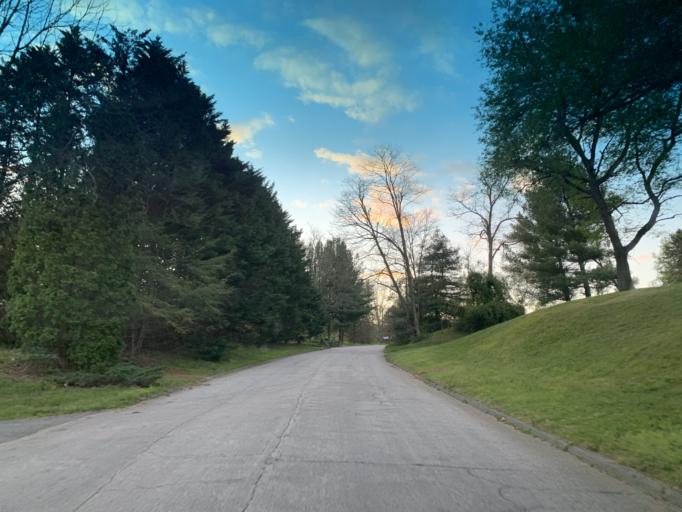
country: US
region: Pennsylvania
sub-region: York County
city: Susquehanna Trails
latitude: 39.6861
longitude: -76.3502
